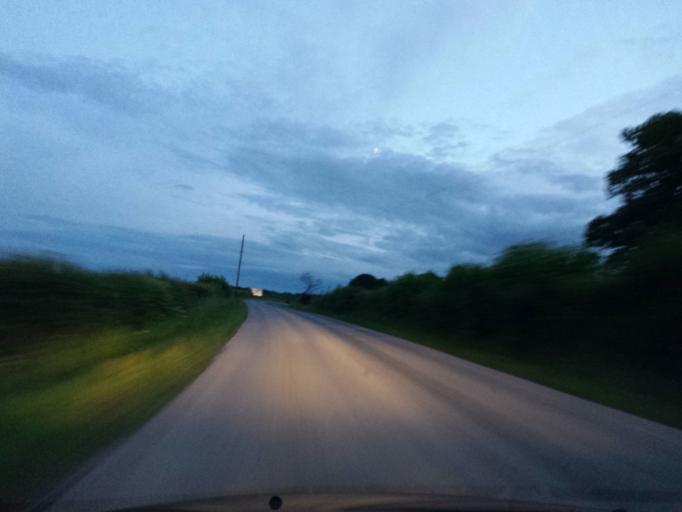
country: GB
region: Scotland
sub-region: The Scottish Borders
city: Duns
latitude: 55.7553
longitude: -2.4018
